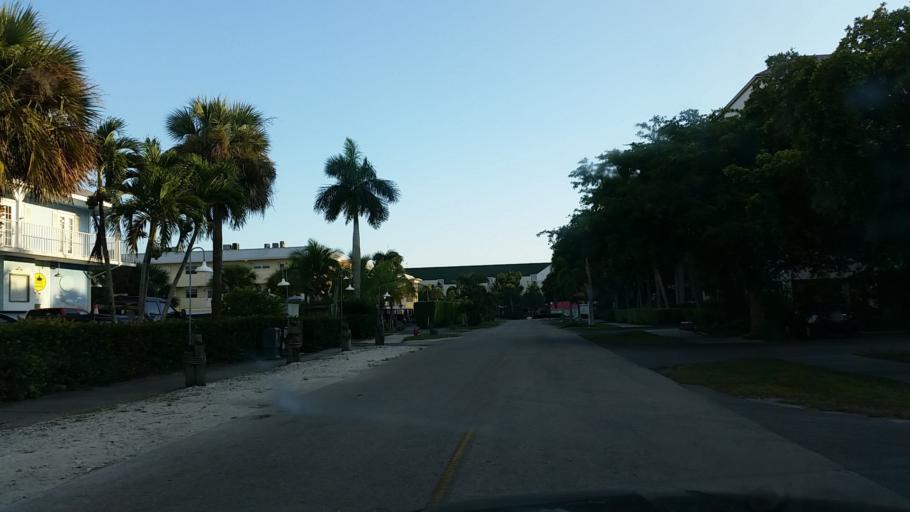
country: US
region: Florida
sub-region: Collier County
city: Naples
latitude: 26.1403
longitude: -81.7922
